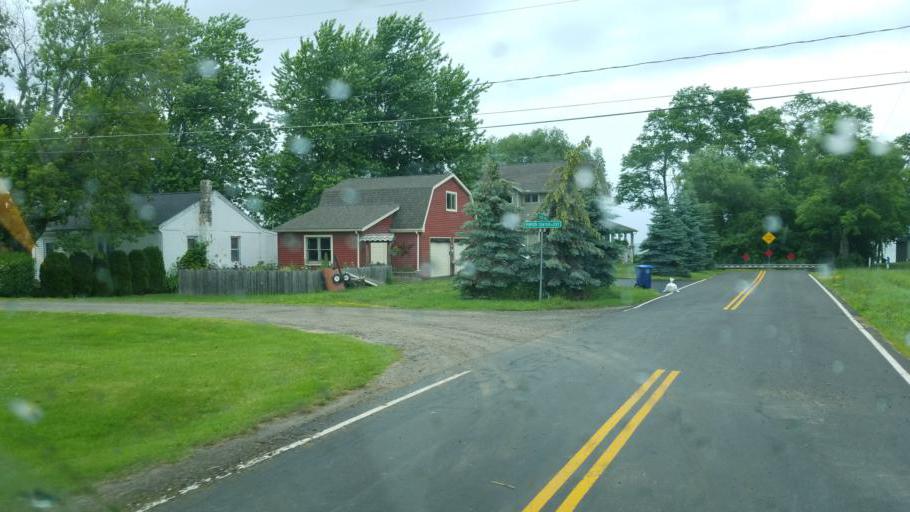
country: US
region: New York
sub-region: Niagara County
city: Ransomville
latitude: 43.2853
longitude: -78.9528
